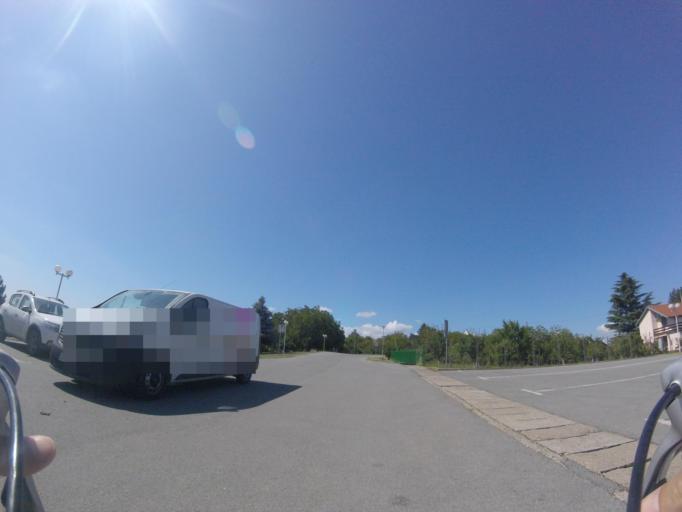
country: HR
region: Osjecko-Baranjska
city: Batina
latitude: 45.8541
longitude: 18.8473
